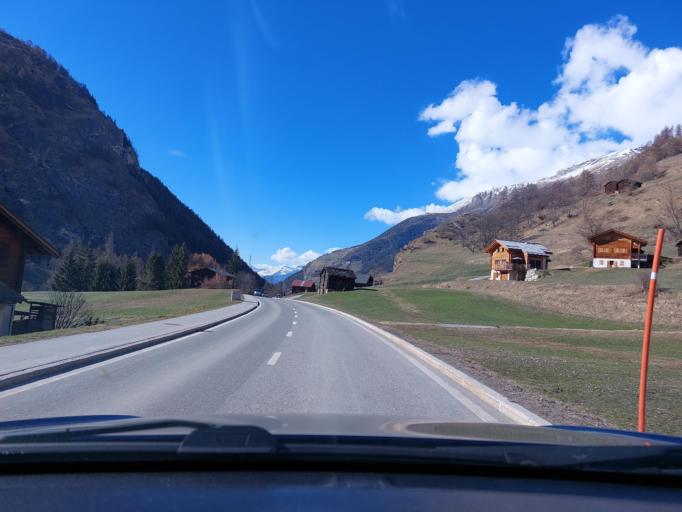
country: CH
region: Valais
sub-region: Herens District
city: Evolene
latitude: 46.0924
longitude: 7.5080
